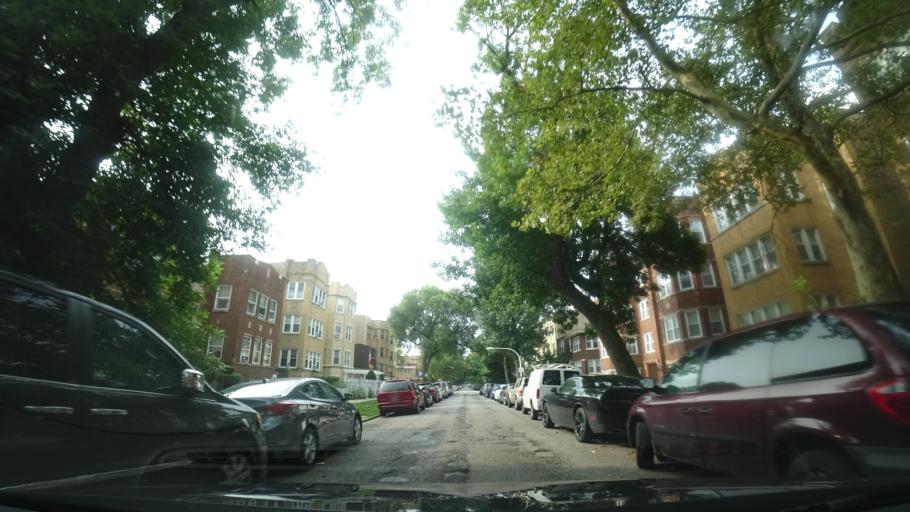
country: US
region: Illinois
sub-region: Cook County
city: Lincolnwood
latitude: 41.9950
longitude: -87.6886
